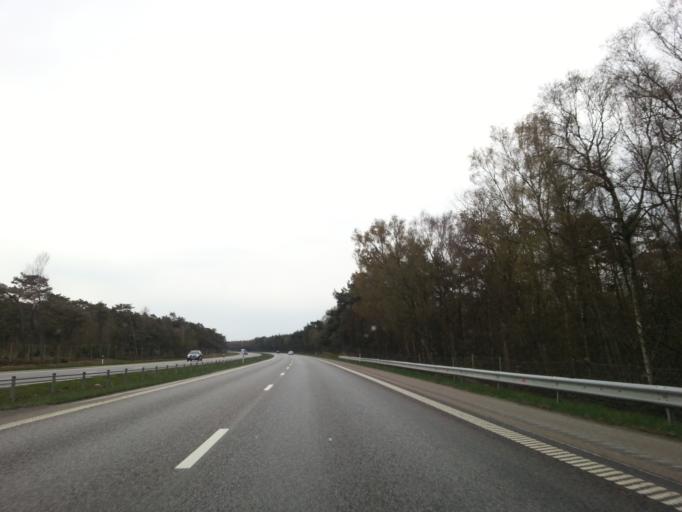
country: SE
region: Halland
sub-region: Halmstads Kommun
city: Paarp
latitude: 56.5749
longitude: 12.9485
